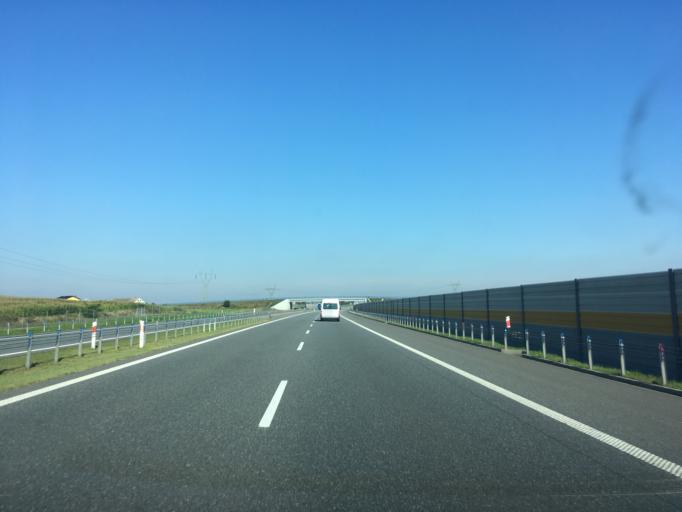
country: PL
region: Kujawsko-Pomorskie
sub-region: Powiat chelminski
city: Lisewo
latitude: 53.2268
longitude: 18.7290
